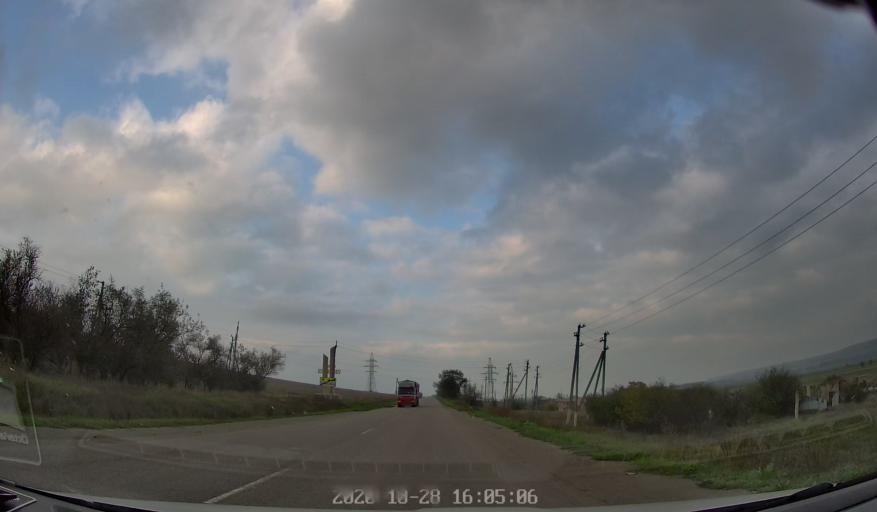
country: UA
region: Odessa
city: Zaliznychne
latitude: 45.8225
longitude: 28.5749
